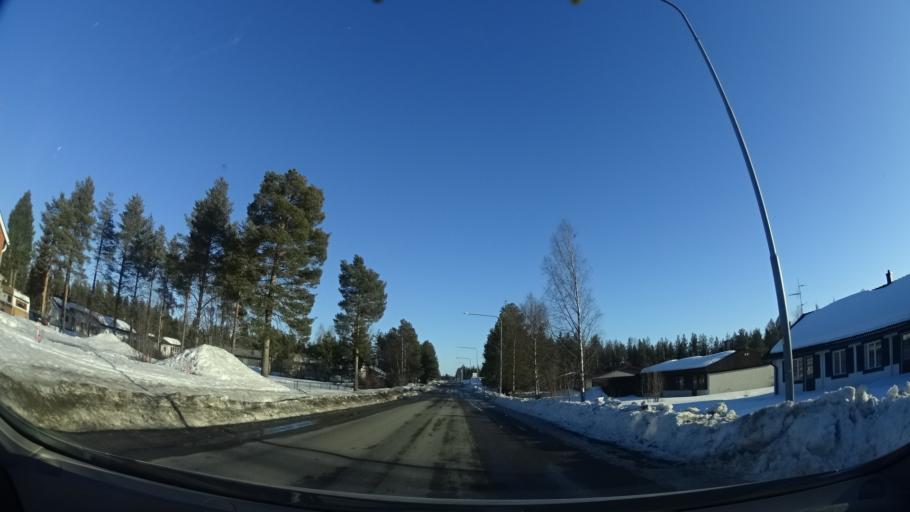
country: SE
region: Vaesterbotten
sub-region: Skelleftea Kommun
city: Langsele
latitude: 65.0564
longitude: 20.0491
